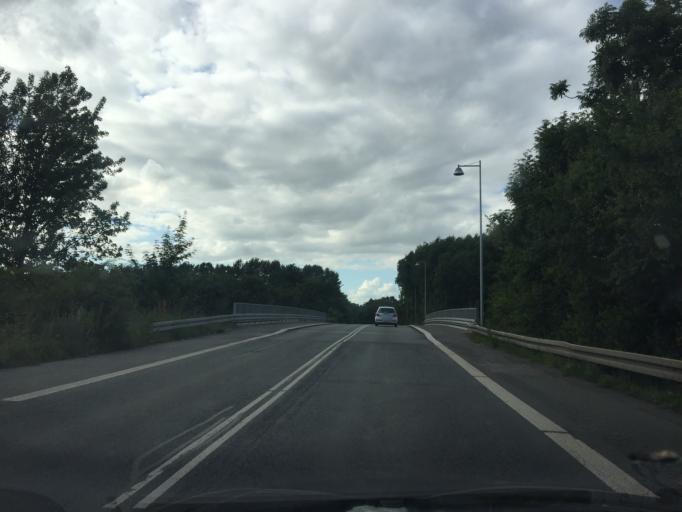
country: DK
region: Capital Region
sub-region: Albertslund Kommune
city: Albertslund
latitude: 55.6584
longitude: 12.3632
